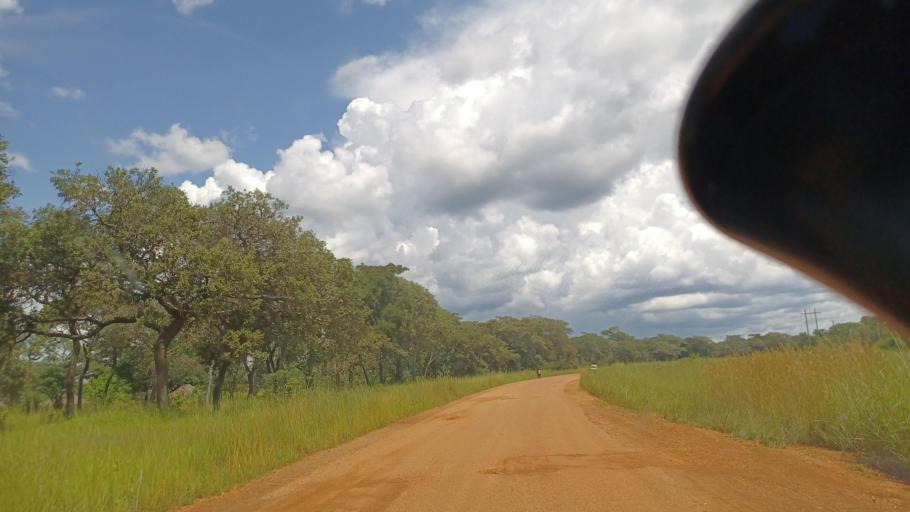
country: ZM
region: North-Western
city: Solwezi
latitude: -12.6942
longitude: 26.0401
